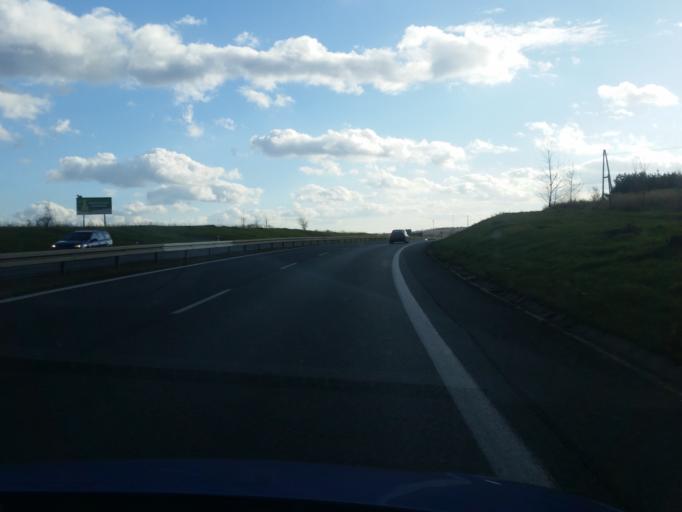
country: PL
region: Silesian Voivodeship
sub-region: Powiat myszkowski
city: Kozieglowy
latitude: 50.5835
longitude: 19.1639
